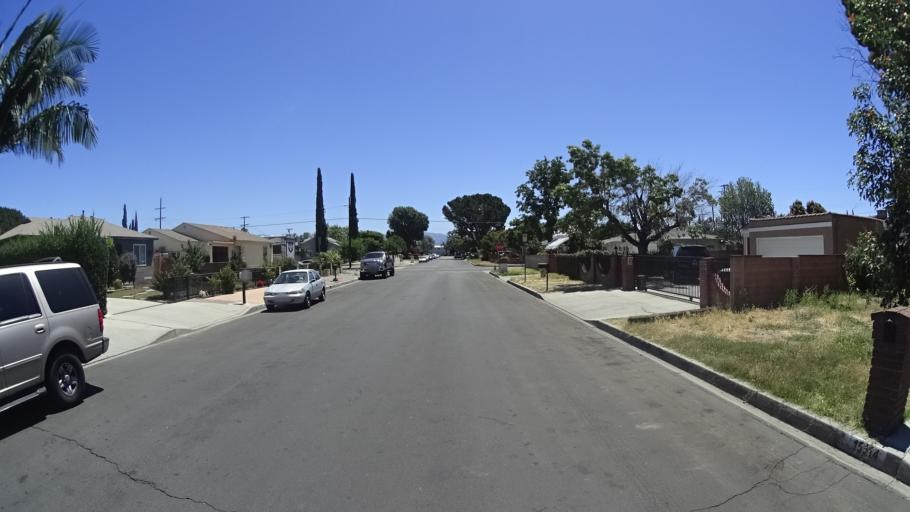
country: US
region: California
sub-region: Los Angeles County
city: San Fernando
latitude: 34.2545
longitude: -118.4703
